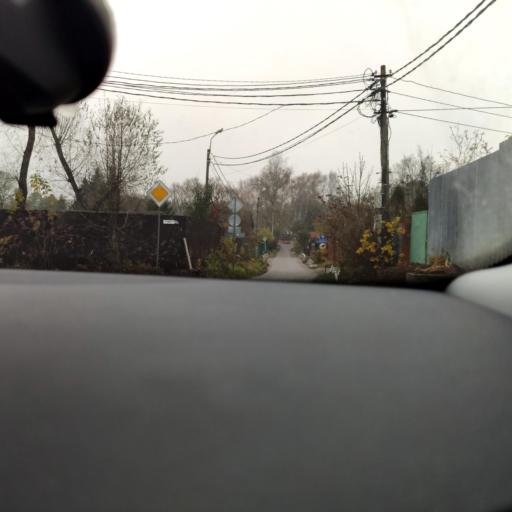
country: RU
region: Moskovskaya
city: Nakhabino
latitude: 55.8507
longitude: 37.1633
